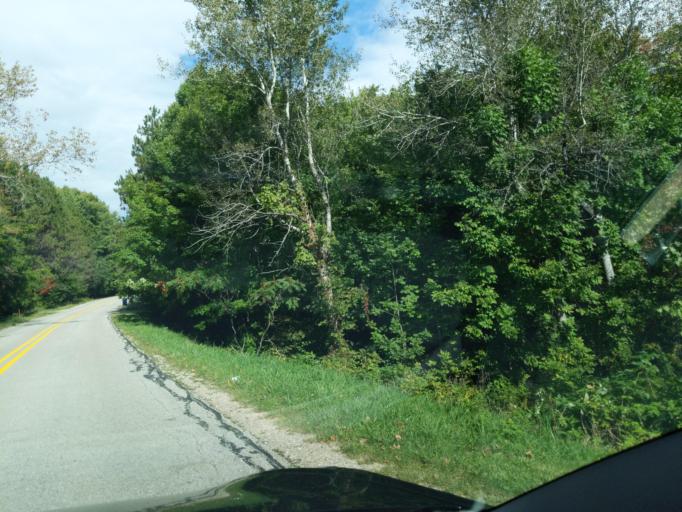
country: US
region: Michigan
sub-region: Antrim County
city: Bellaire
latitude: 44.9692
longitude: -85.3237
